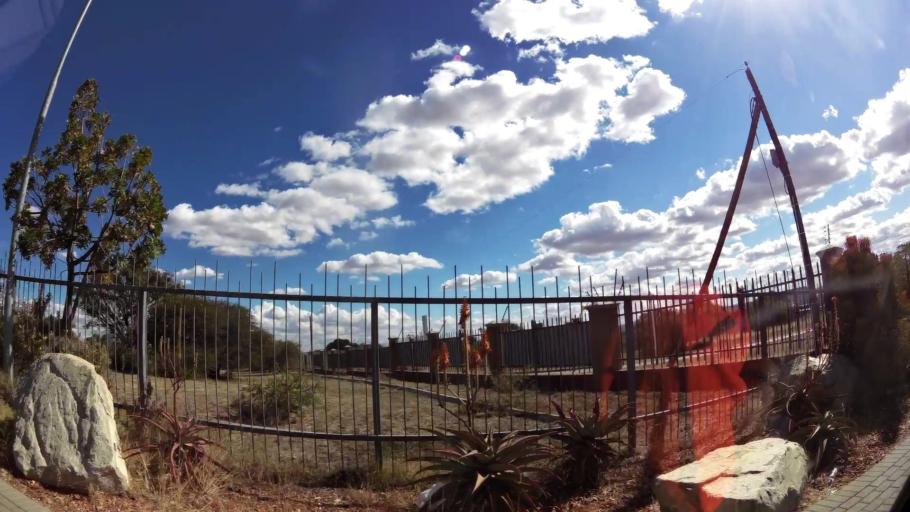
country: ZA
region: Limpopo
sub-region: Capricorn District Municipality
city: Polokwane
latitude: -23.8695
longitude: 29.5094
